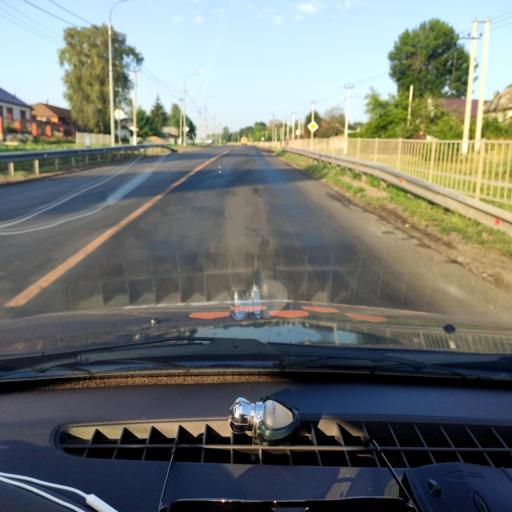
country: RU
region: Lipetsk
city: Izmalkovo
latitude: 52.4793
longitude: 38.0353
